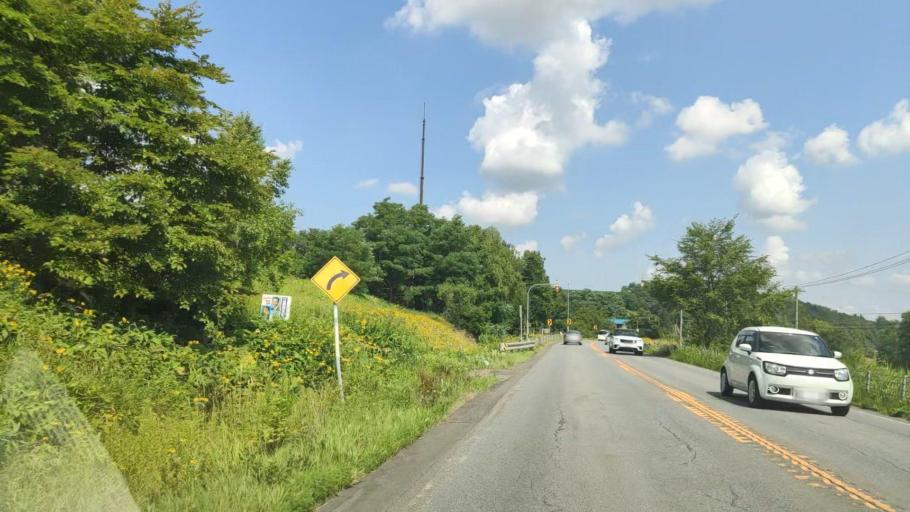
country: JP
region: Hokkaido
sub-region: Asahikawa-shi
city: Asahikawa
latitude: 43.5637
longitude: 142.4347
